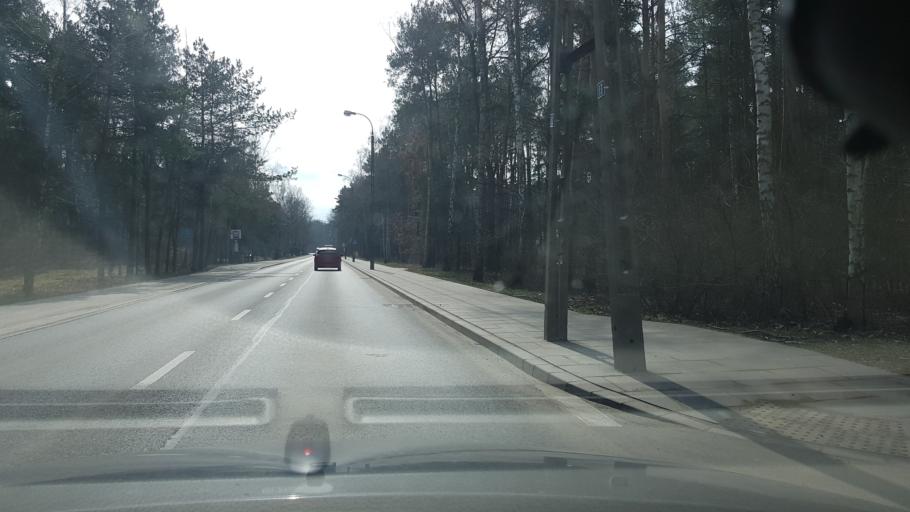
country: PL
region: Masovian Voivodeship
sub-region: Warszawa
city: Wesola
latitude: 52.2403
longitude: 21.2224
